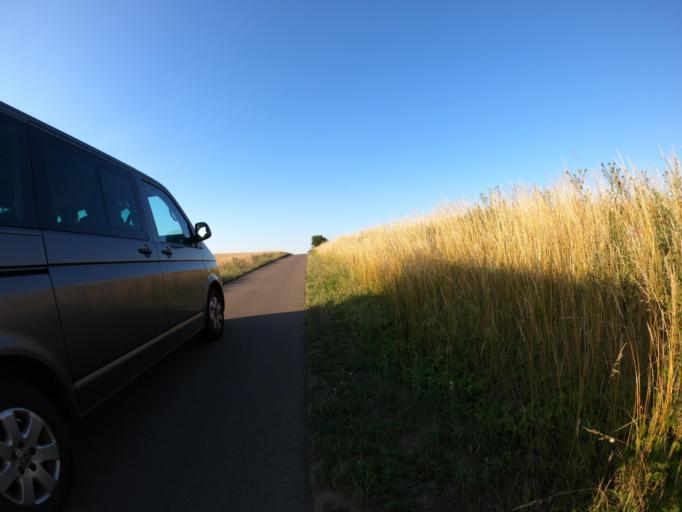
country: DE
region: Brandenburg
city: Tantow
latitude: 53.2845
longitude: 14.3663
